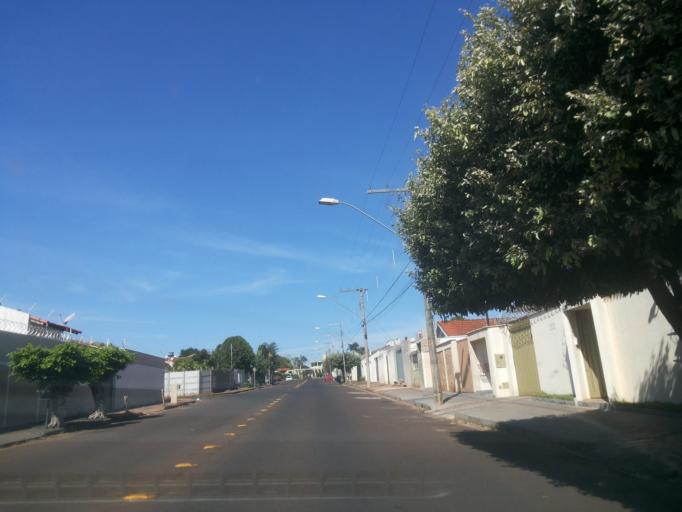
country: BR
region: Minas Gerais
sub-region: Ituiutaba
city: Ituiutaba
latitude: -18.9863
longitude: -49.4610
